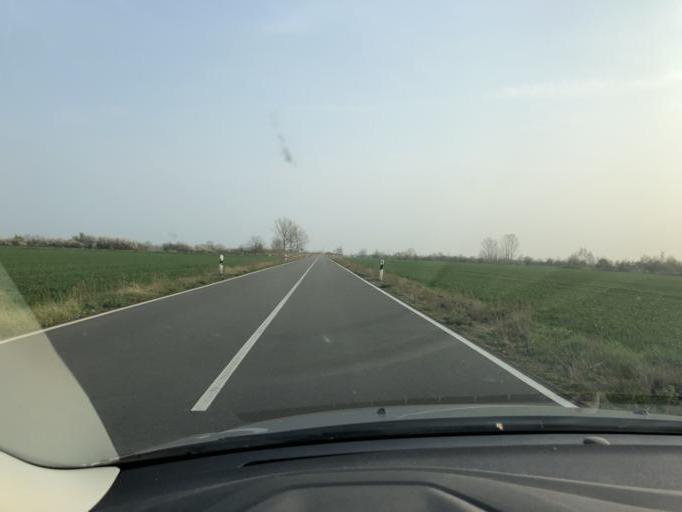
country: DE
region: Saxony
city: Dobernitz
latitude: 51.5061
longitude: 12.3134
